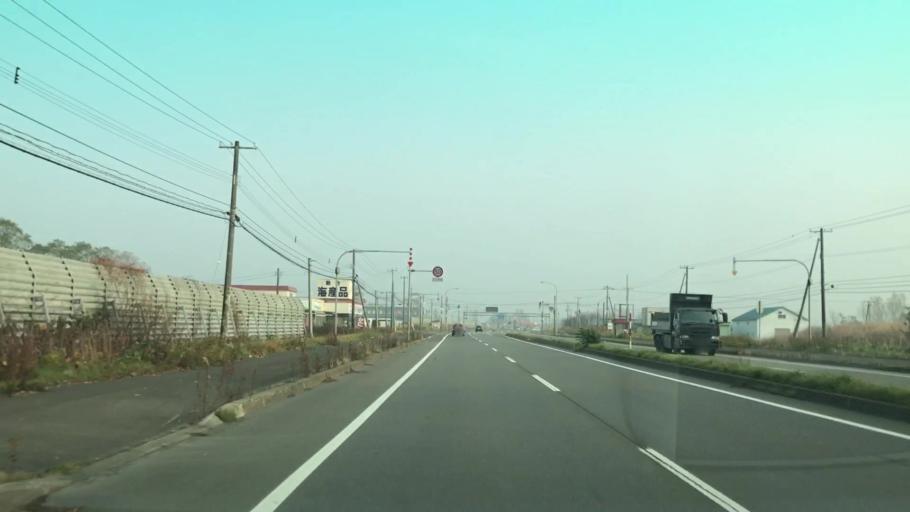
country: JP
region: Hokkaido
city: Ishikari
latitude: 43.2117
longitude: 141.3344
